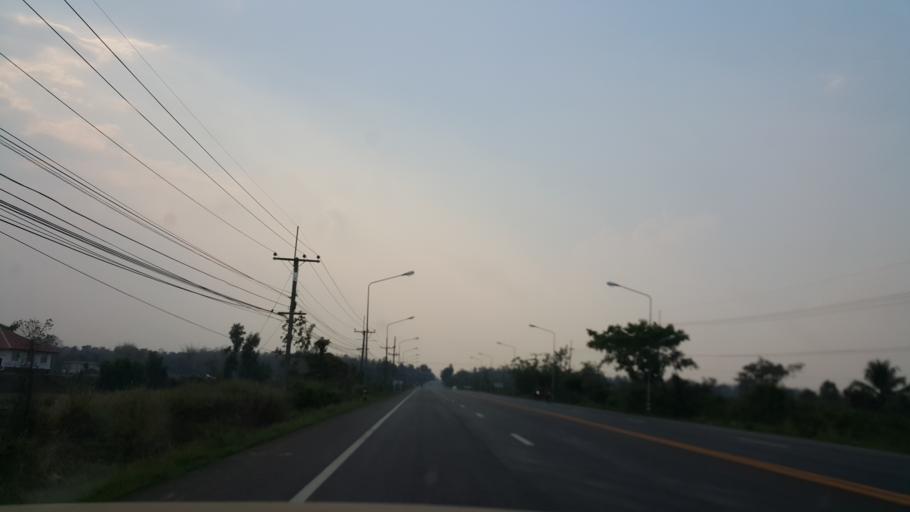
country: TH
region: Nakhon Phanom
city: Renu Nakhon
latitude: 17.0242
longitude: 104.7172
